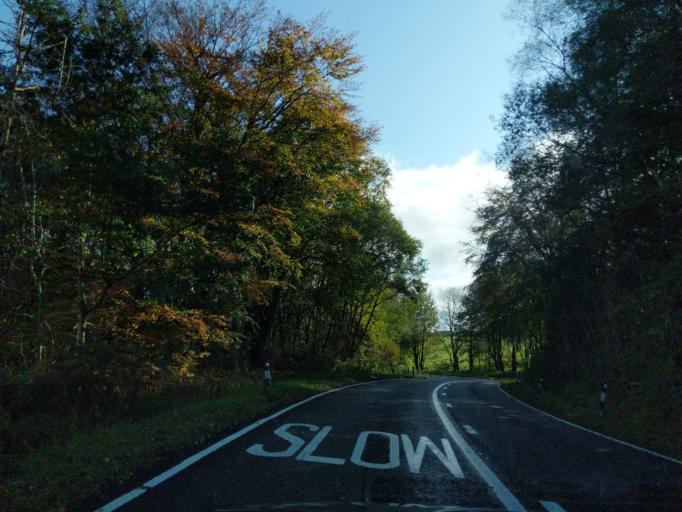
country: GB
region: Scotland
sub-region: Dumfries and Galloway
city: Moffat
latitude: 55.3418
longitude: -3.4590
